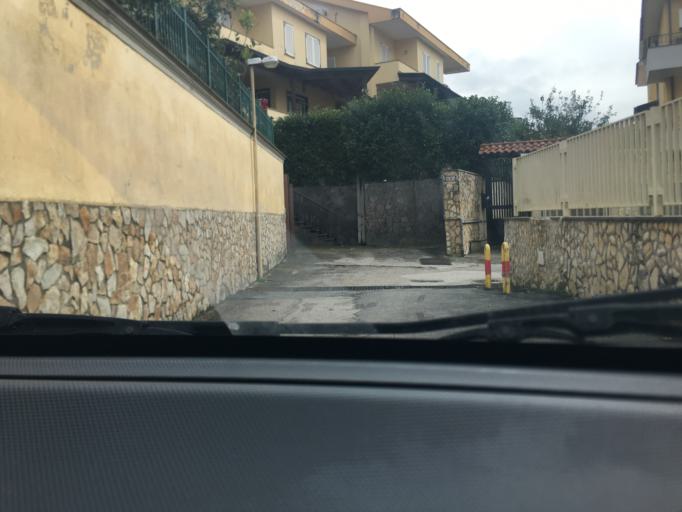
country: IT
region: Campania
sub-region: Provincia di Napoli
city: Marano di Napoli
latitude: 40.8907
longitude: 14.1768
